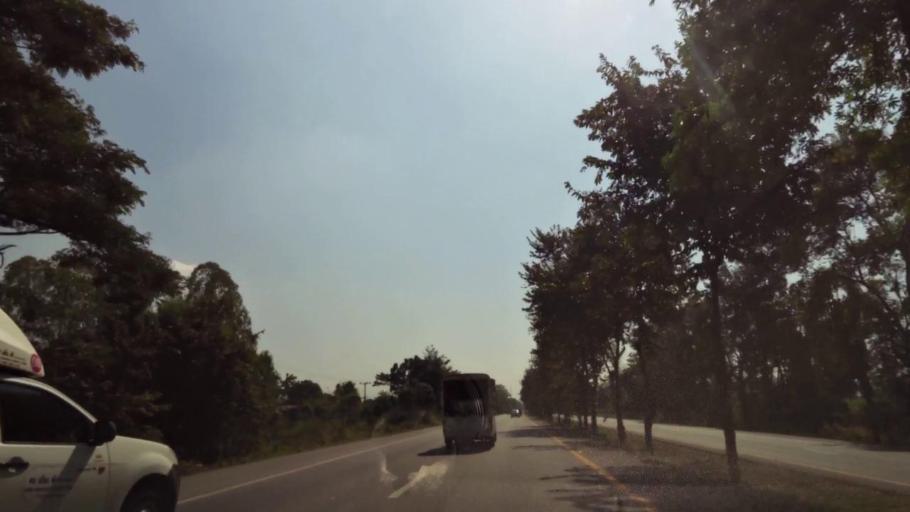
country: TH
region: Phichit
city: Bueng Na Rang
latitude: 16.1072
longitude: 100.1258
